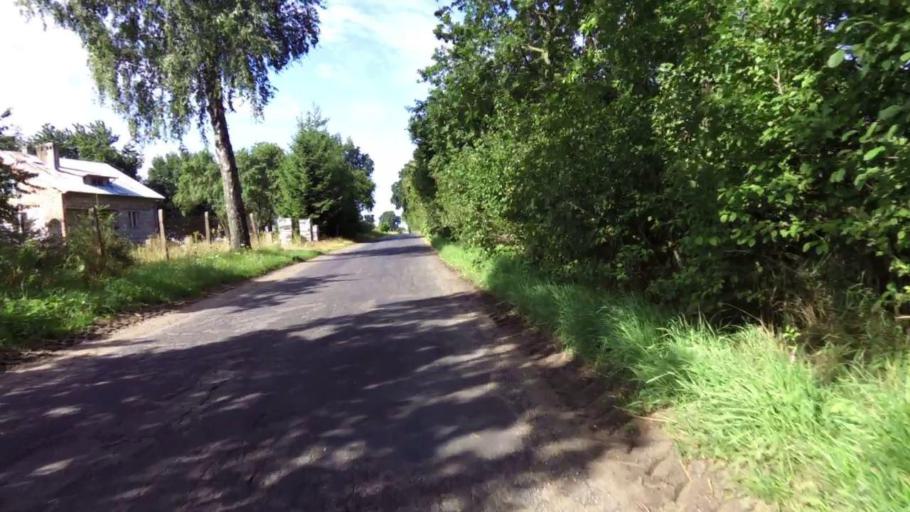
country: PL
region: West Pomeranian Voivodeship
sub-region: Powiat stargardzki
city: Marianowo
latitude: 53.3628
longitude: 15.2282
